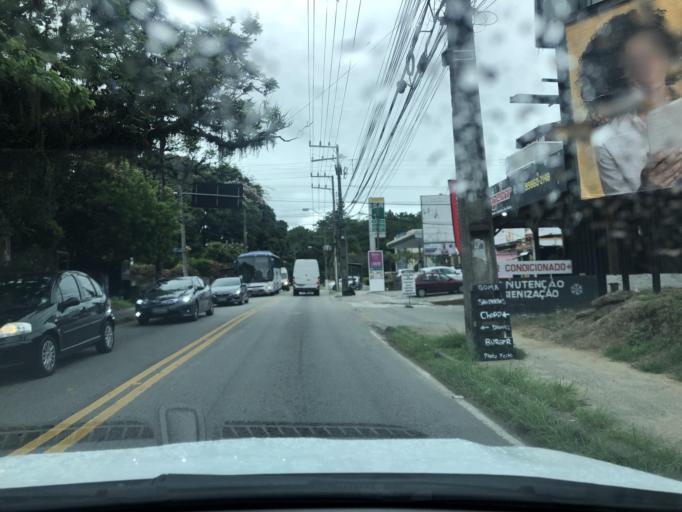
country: BR
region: Santa Catarina
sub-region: Florianopolis
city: Pantanal
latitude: -27.6105
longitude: -48.5238
